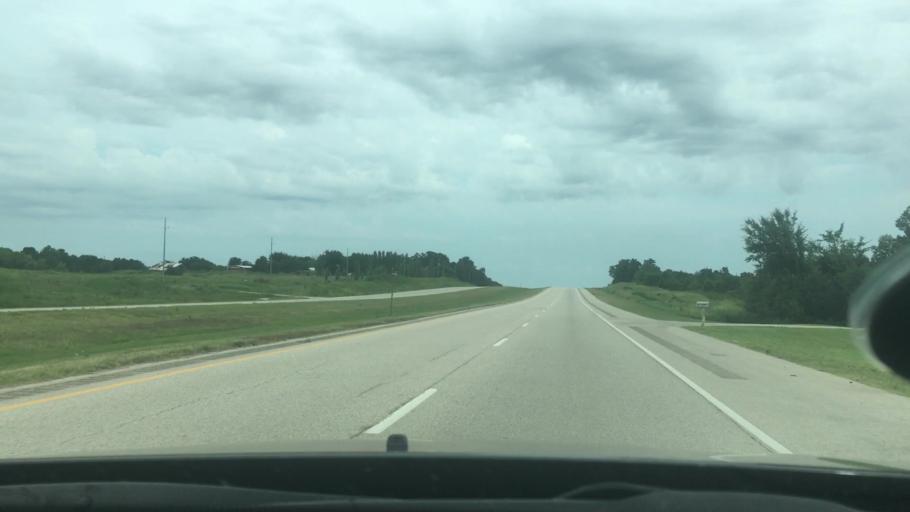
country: US
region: Oklahoma
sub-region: Pontotoc County
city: Byng
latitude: 34.9131
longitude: -96.6796
